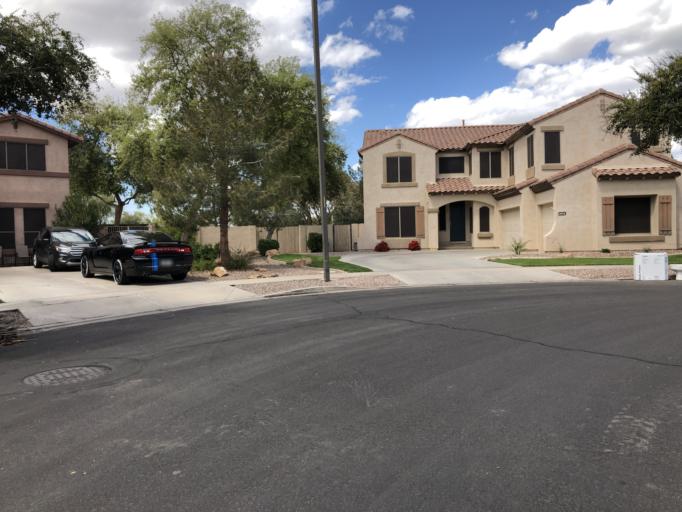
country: US
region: Arizona
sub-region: Maricopa County
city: Queen Creek
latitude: 33.2704
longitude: -111.6921
